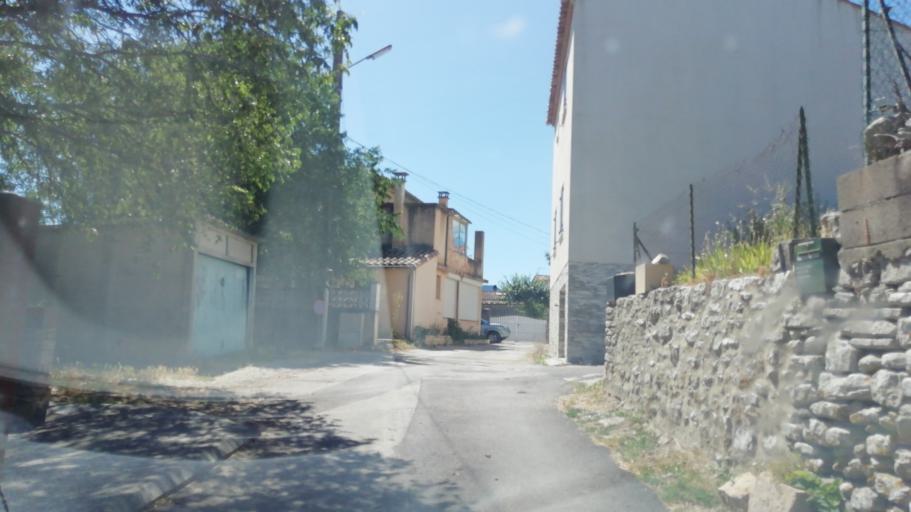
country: FR
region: Languedoc-Roussillon
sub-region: Departement de l'Herault
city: Saint-Martin-de-Londres
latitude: 43.8271
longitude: 3.7772
